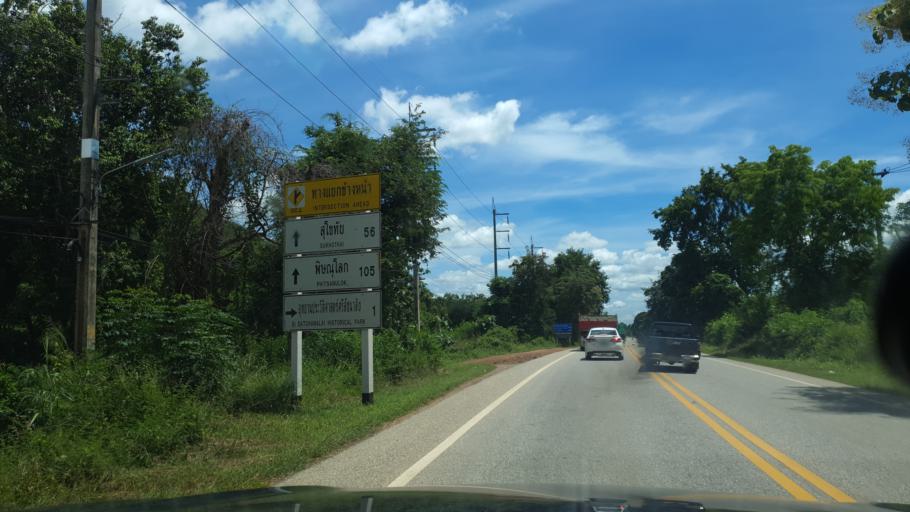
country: TH
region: Sukhothai
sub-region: Amphoe Si Satchanalai
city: Si Satchanalai
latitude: 17.4392
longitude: 99.7987
